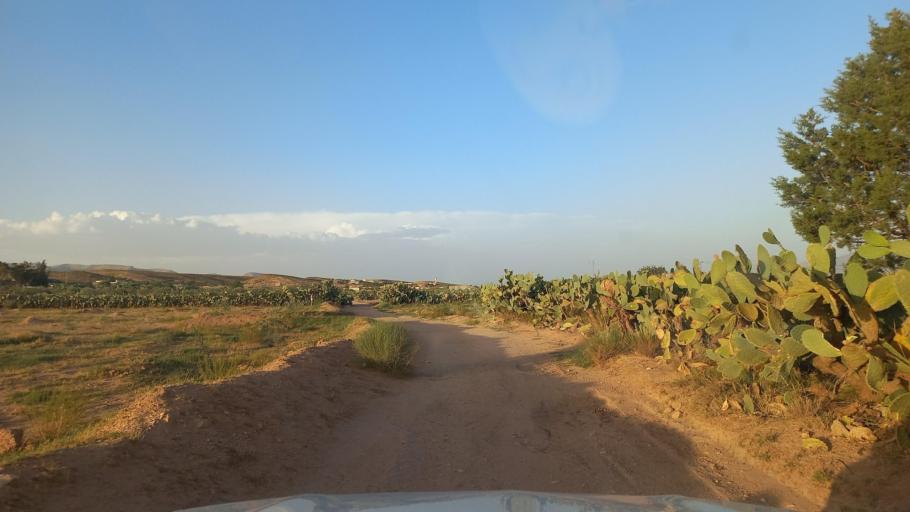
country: TN
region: Al Qasrayn
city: Sbiba
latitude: 35.3724
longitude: 9.0081
